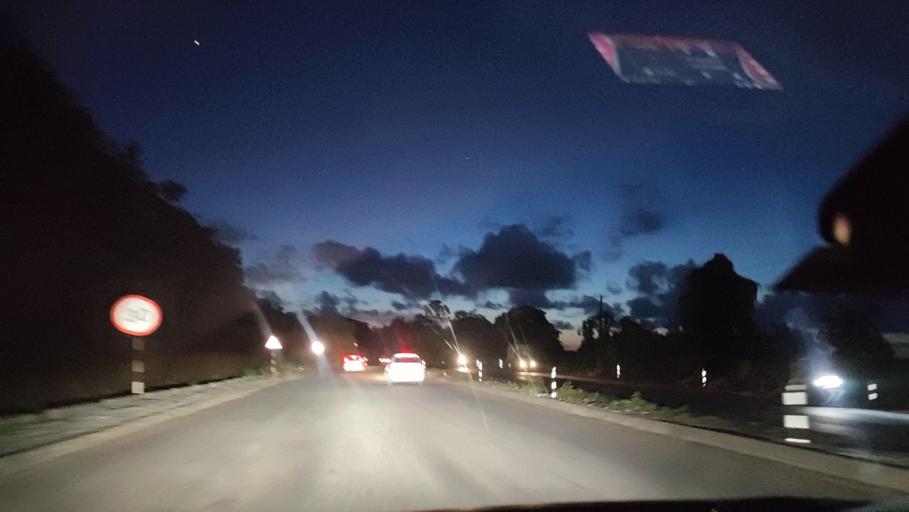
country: IN
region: Karnataka
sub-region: Uttar Kannada
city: Kumta
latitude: 14.4423
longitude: 74.4420
